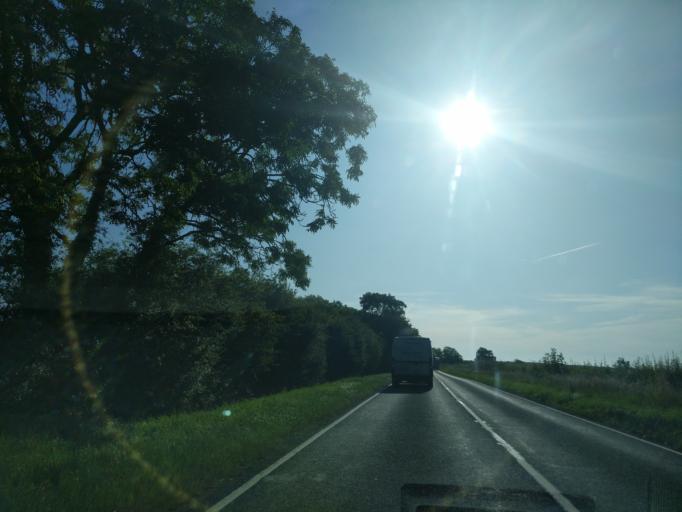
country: GB
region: England
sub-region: District of Rutland
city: Pickworth
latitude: 52.8072
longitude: -0.4898
